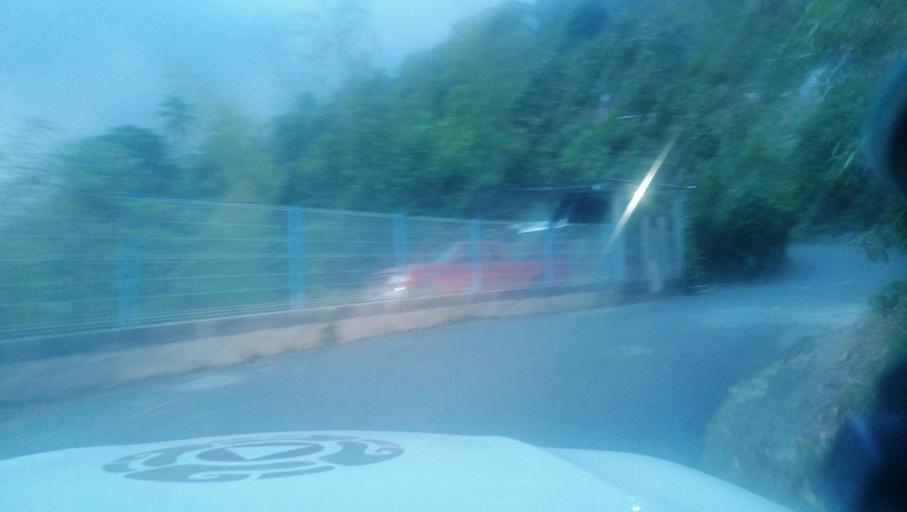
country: MX
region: Chiapas
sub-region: Cacahoatan
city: Benito Juarez
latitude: 15.1188
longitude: -92.2100
